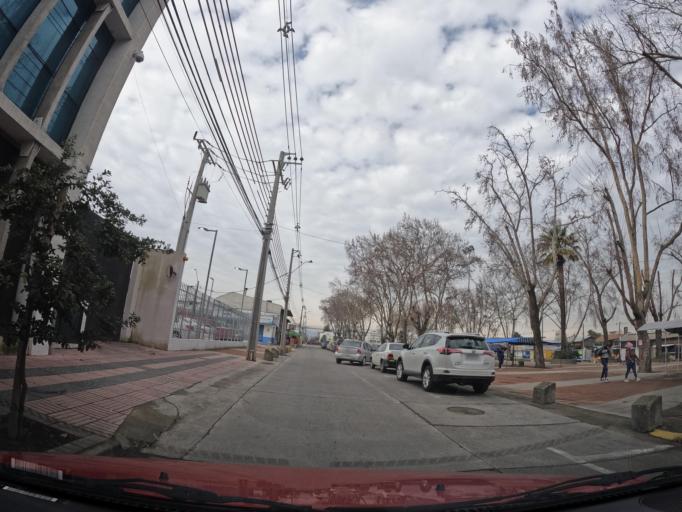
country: CL
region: Maule
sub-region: Provincia de Linares
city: Linares
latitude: -35.8487
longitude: -71.5980
